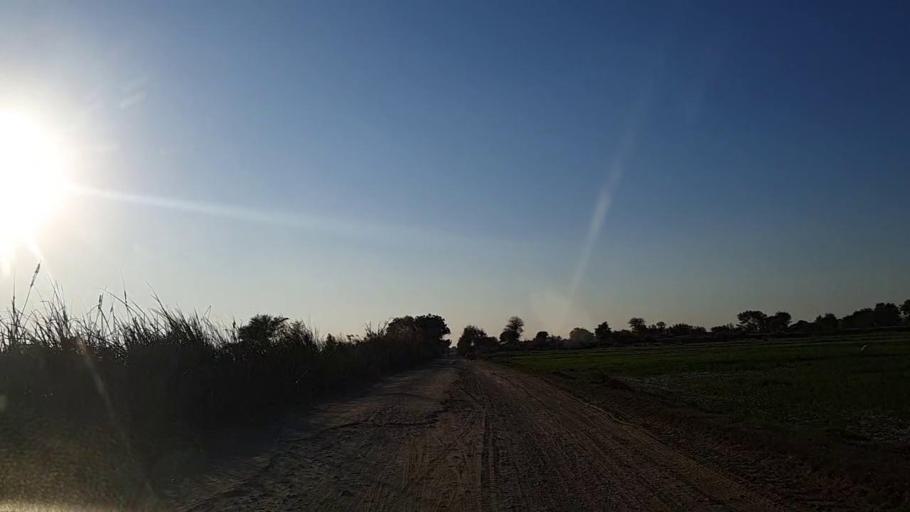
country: PK
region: Sindh
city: Khadro
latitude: 26.2791
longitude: 68.8492
